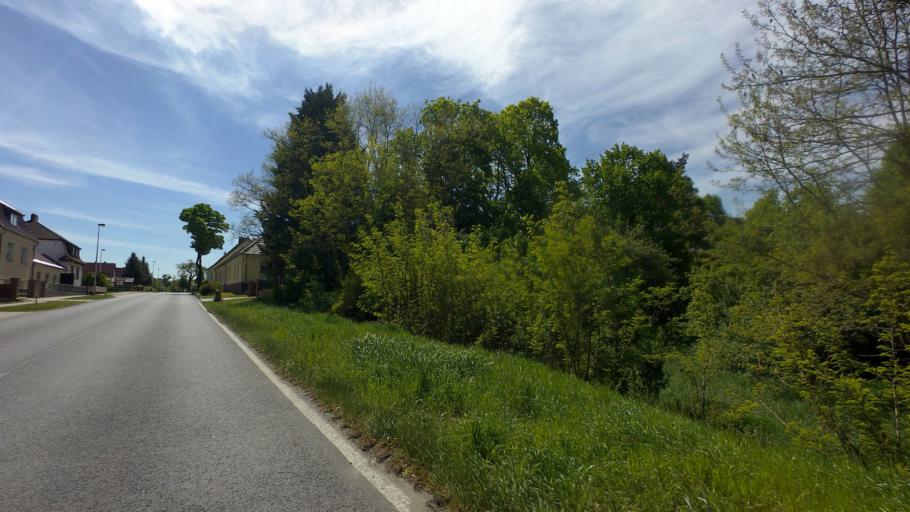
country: DE
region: Brandenburg
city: Luckenwalde
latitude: 52.1626
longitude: 13.0988
